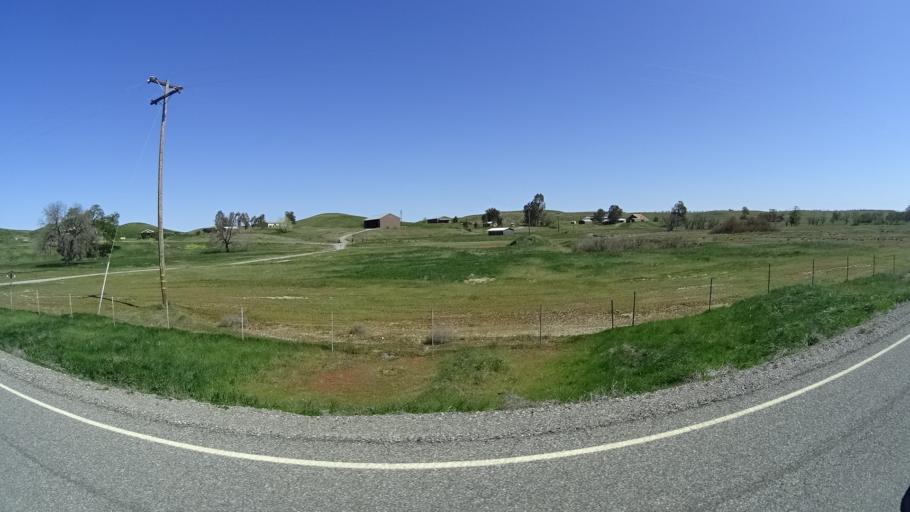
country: US
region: California
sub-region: Glenn County
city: Orland
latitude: 39.8222
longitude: -122.3303
